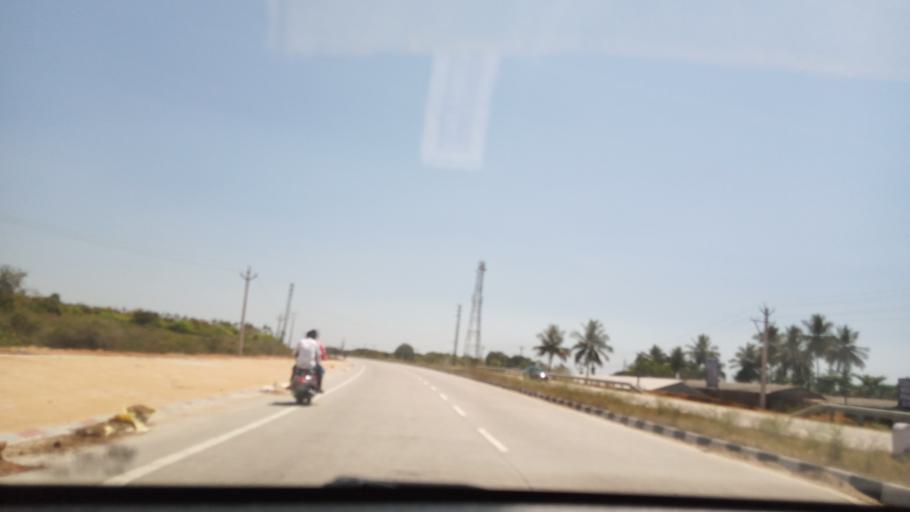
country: IN
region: Andhra Pradesh
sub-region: Chittoor
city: Chittoor
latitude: 13.2012
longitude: 78.9549
